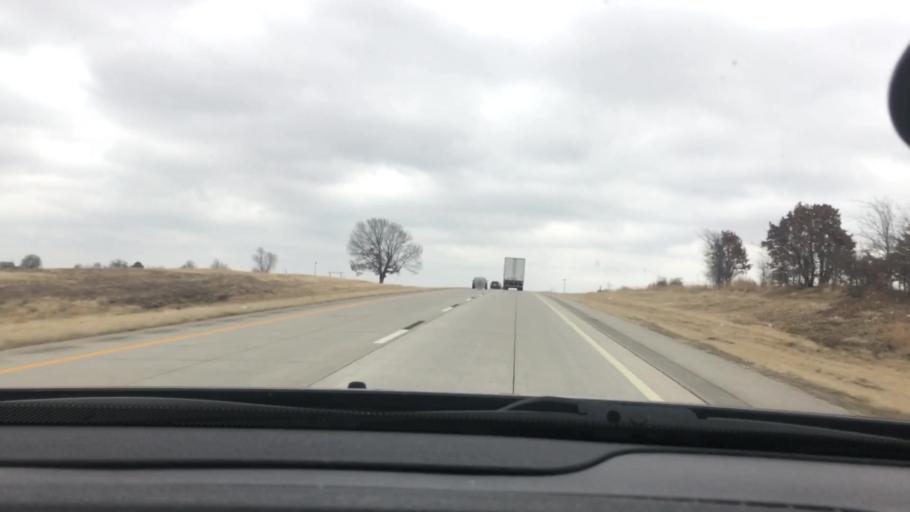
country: US
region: Oklahoma
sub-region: Atoka County
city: Atoka
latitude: 34.2116
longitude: -96.2326
